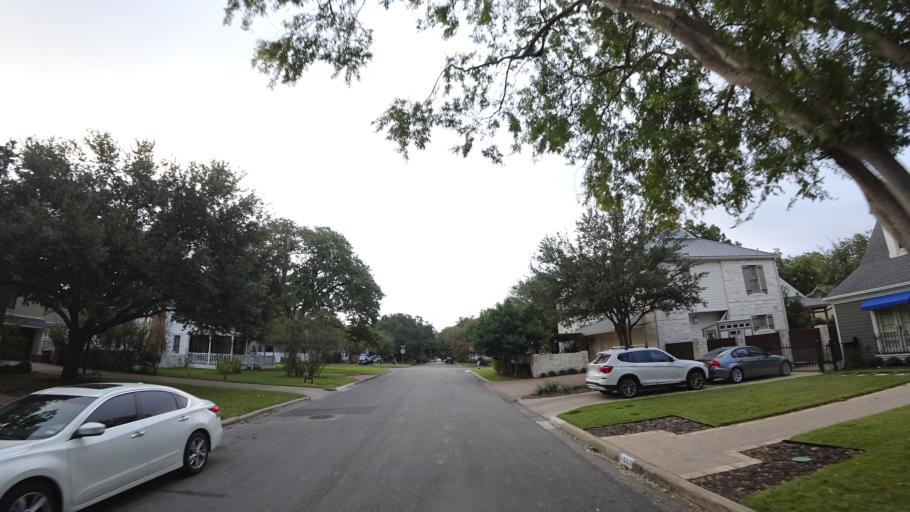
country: US
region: Texas
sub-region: Travis County
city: Austin
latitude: 30.2973
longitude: -97.7546
